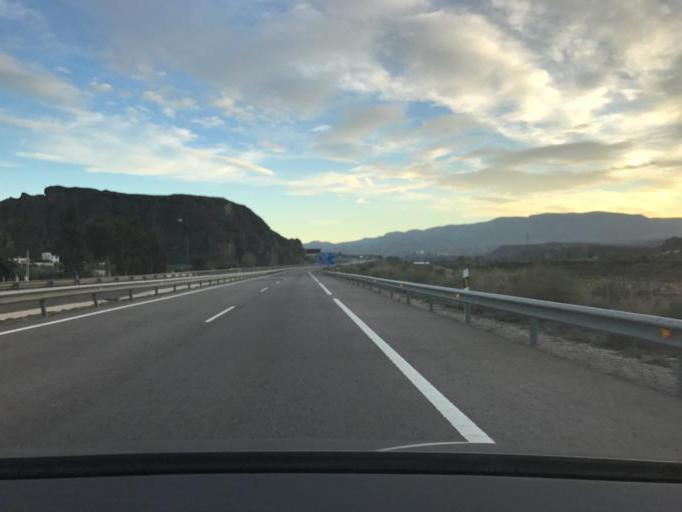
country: ES
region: Andalusia
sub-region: Provincia de Almeria
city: Rioja
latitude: 36.9703
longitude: -2.4653
